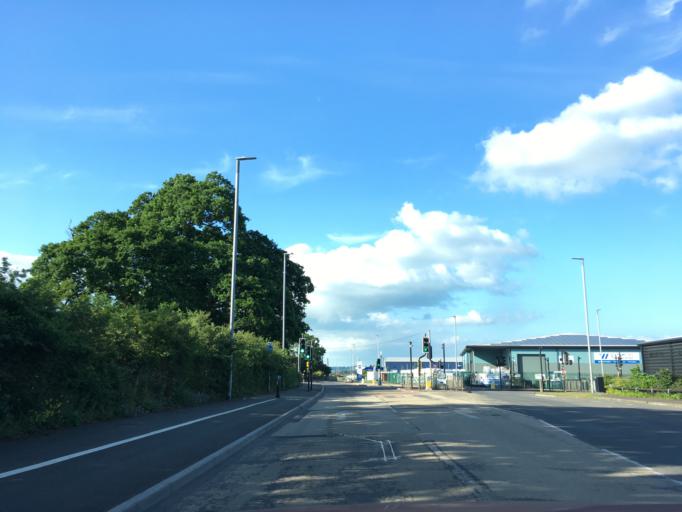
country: GB
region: England
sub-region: Somerset
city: North Petherton
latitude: 51.0985
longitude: -3.0039
